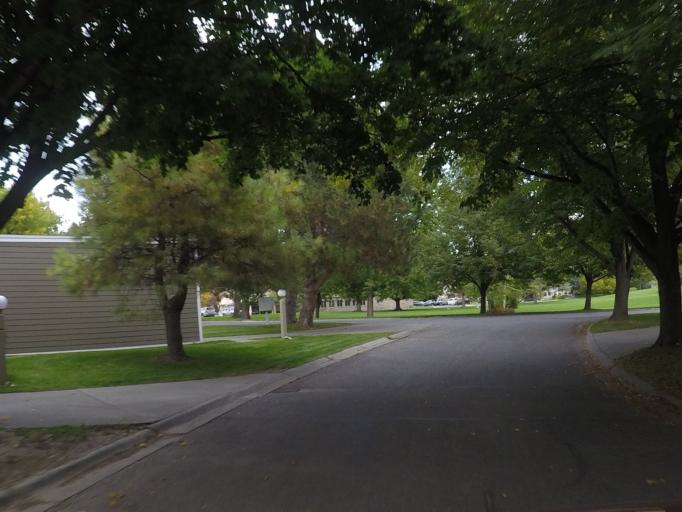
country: US
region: Montana
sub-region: Yellowstone County
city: Billings
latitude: 45.7928
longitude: -108.5558
